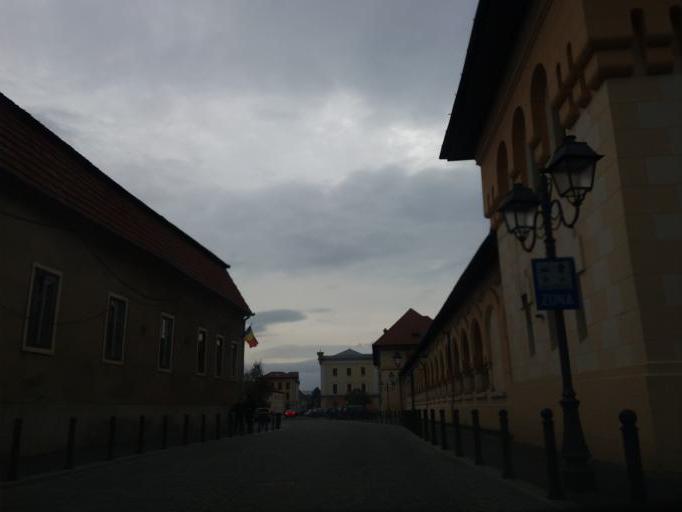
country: RO
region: Alba
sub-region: Municipiul Alba Iulia
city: Alba Iulia
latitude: 46.0689
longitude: 23.5688
